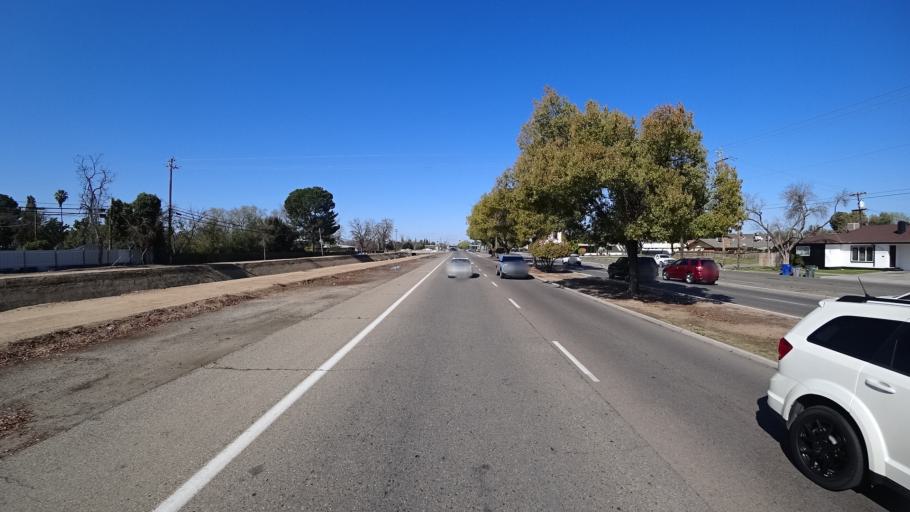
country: US
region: California
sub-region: Fresno County
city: Fresno
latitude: 36.7796
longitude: -119.7789
